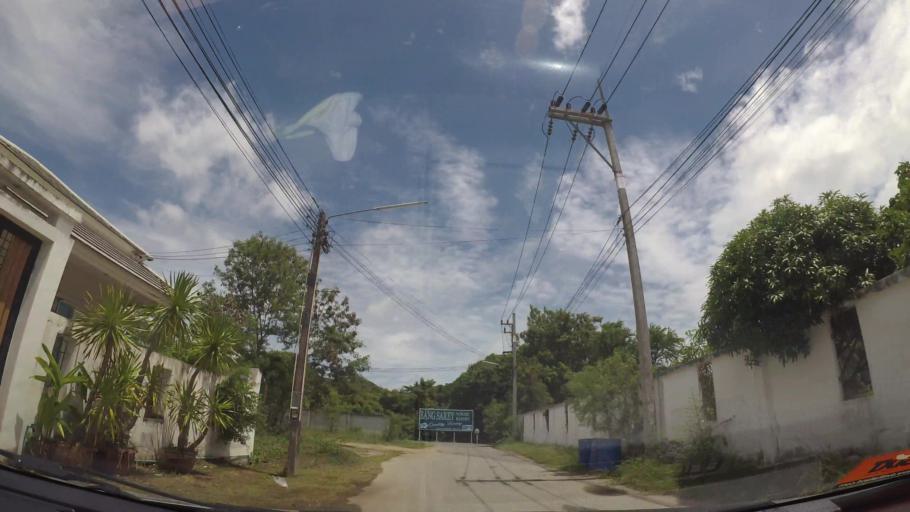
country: TH
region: Chon Buri
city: Sattahip
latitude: 12.7425
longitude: 100.8904
